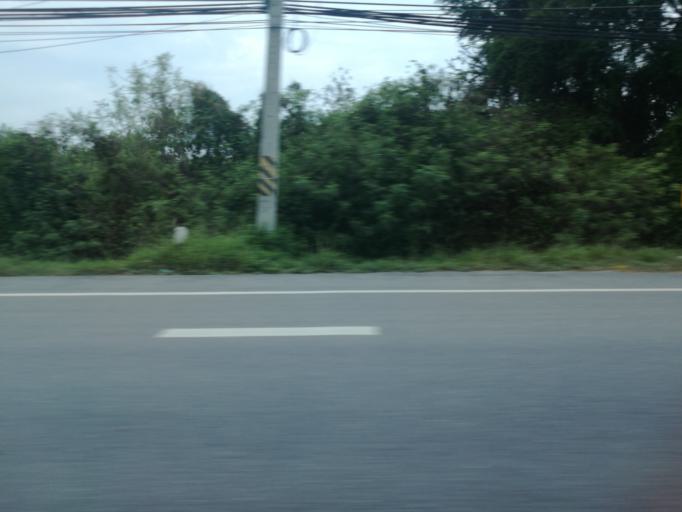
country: TH
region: Prachuap Khiri Khan
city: Pran Buri
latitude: 12.3758
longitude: 99.8878
